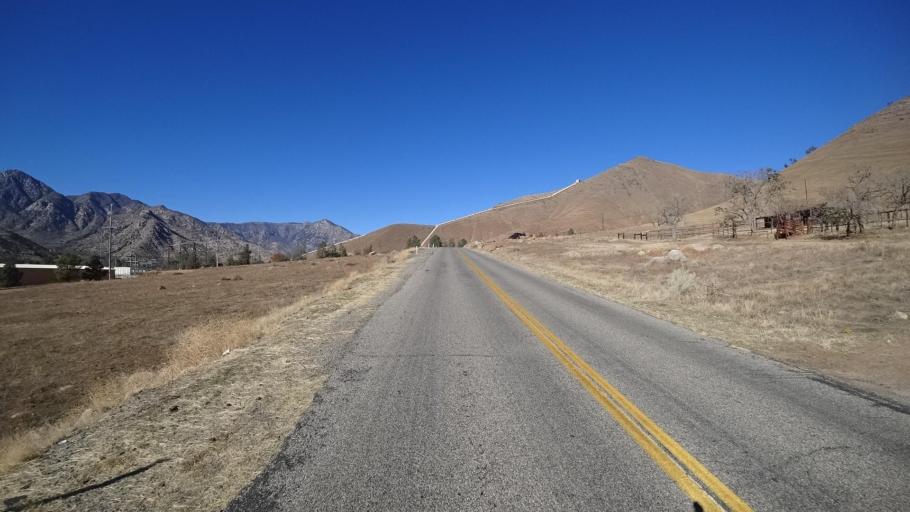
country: US
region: California
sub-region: Kern County
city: Kernville
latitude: 35.7724
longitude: -118.4307
